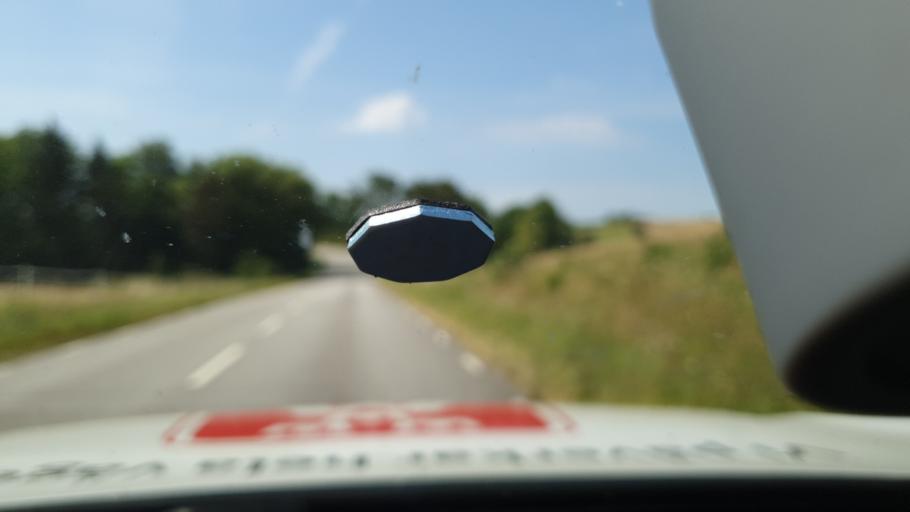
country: SE
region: Skane
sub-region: Svedala Kommun
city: Svedala
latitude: 55.4989
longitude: 13.1888
